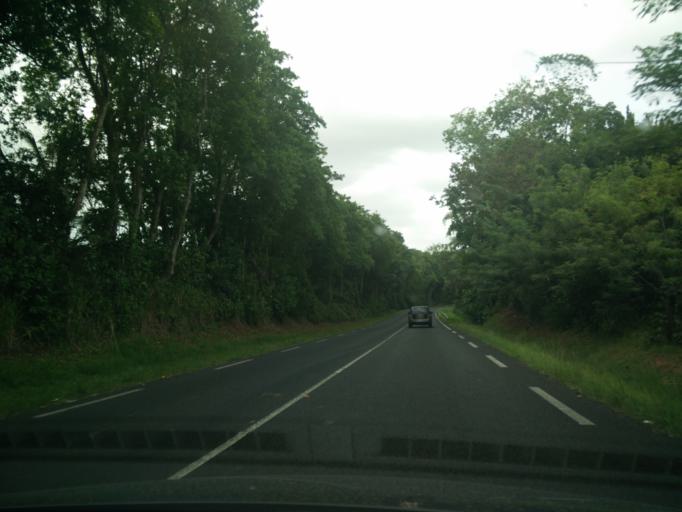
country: GP
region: Guadeloupe
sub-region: Guadeloupe
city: Petit-Bourg
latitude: 16.1990
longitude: -61.6427
